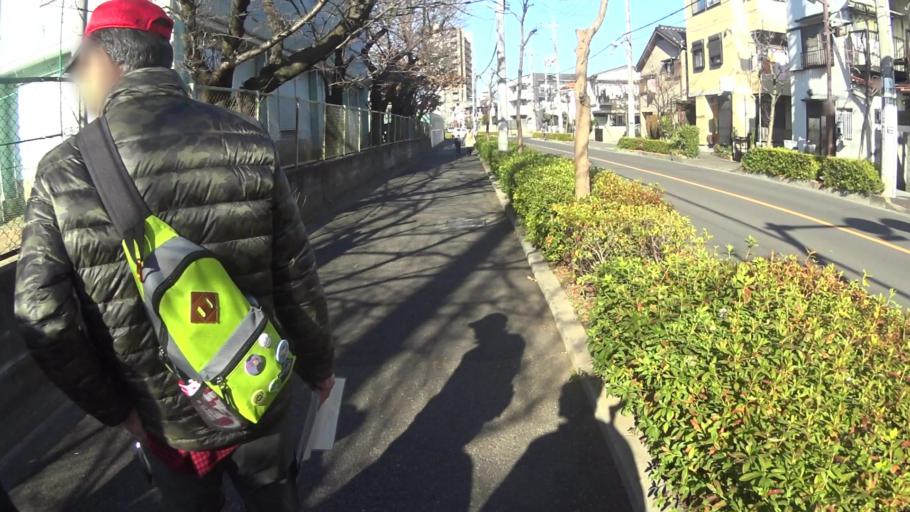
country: JP
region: Saitama
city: Shimotoda
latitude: 35.8529
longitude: 139.6691
